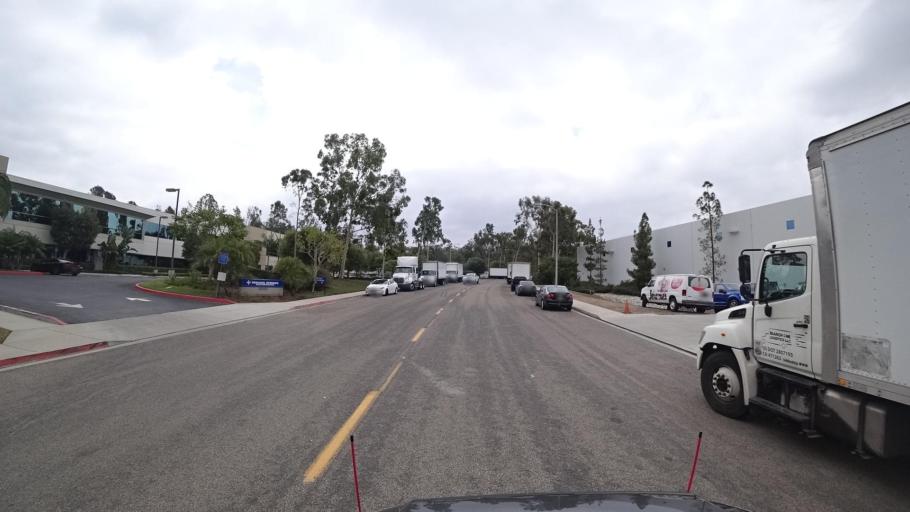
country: US
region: California
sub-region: San Diego County
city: Fairbanks Ranch
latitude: 33.0164
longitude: -117.1043
